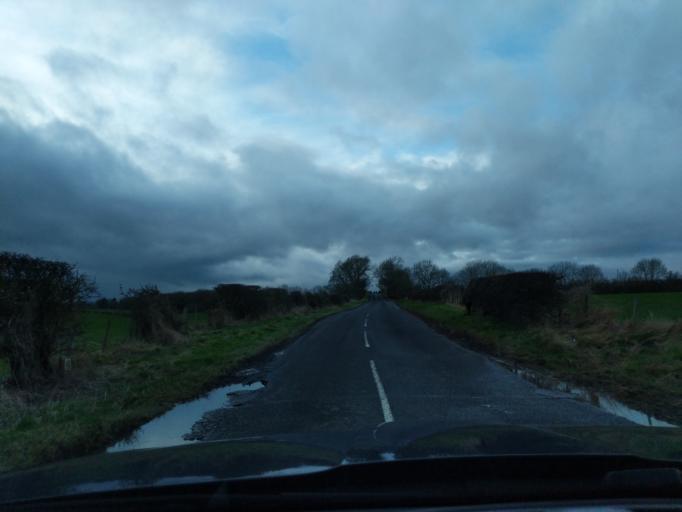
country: GB
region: England
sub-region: Northumberland
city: Ford
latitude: 55.7154
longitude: -2.1332
